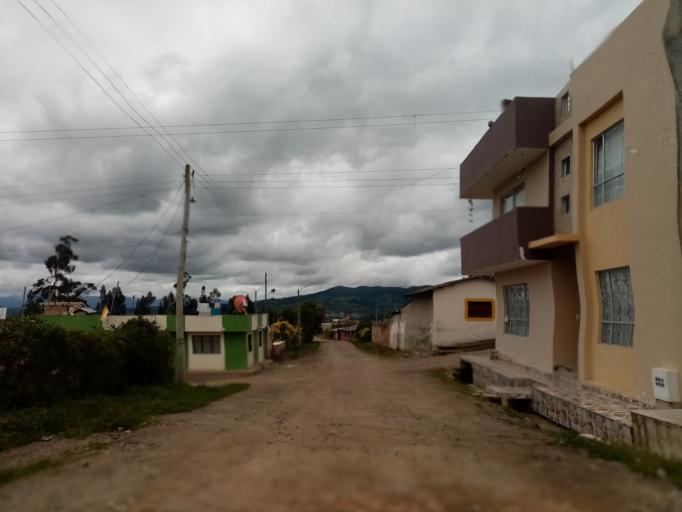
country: CO
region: Narino
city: Tuquerres
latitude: 1.0672
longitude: -77.6555
